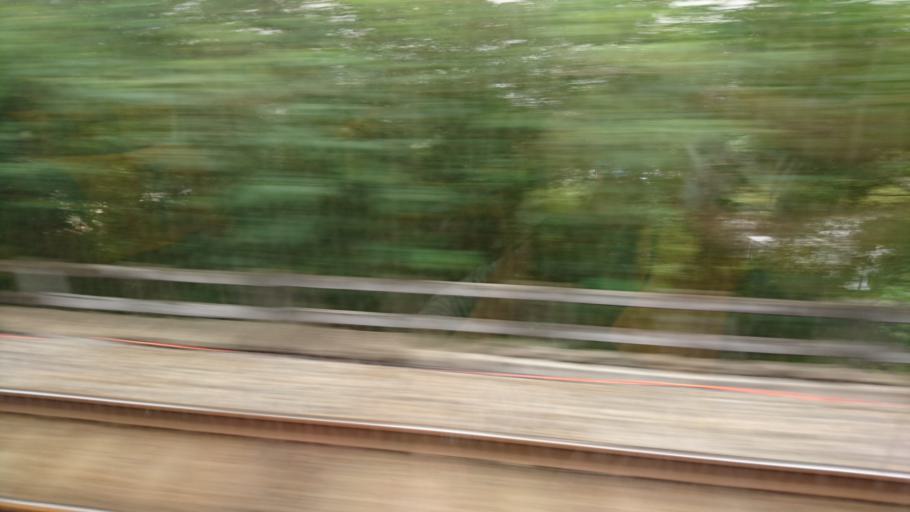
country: TW
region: Taiwan
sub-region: Hsinchu
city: Zhubei
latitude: 24.8548
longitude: 121.0083
